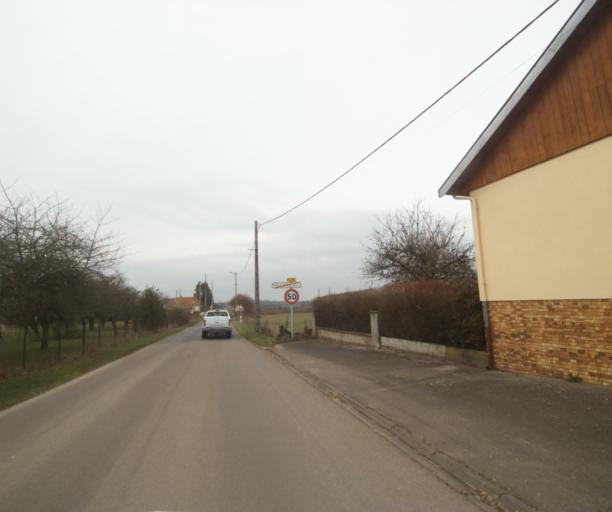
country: FR
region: Champagne-Ardenne
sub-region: Departement de la Haute-Marne
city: Villiers-en-Lieu
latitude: 48.6665
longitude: 4.8947
